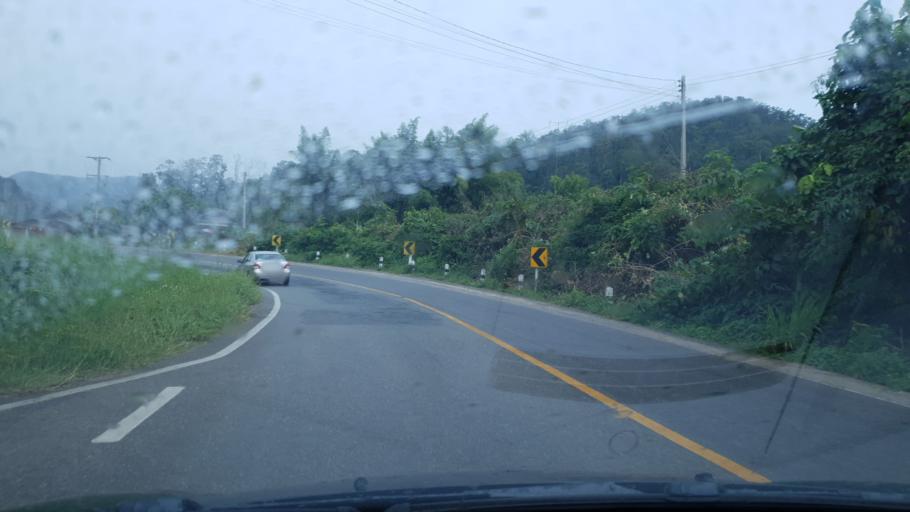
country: TH
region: Mae Hong Son
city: Khun Yuam
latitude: 18.6975
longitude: 97.9185
